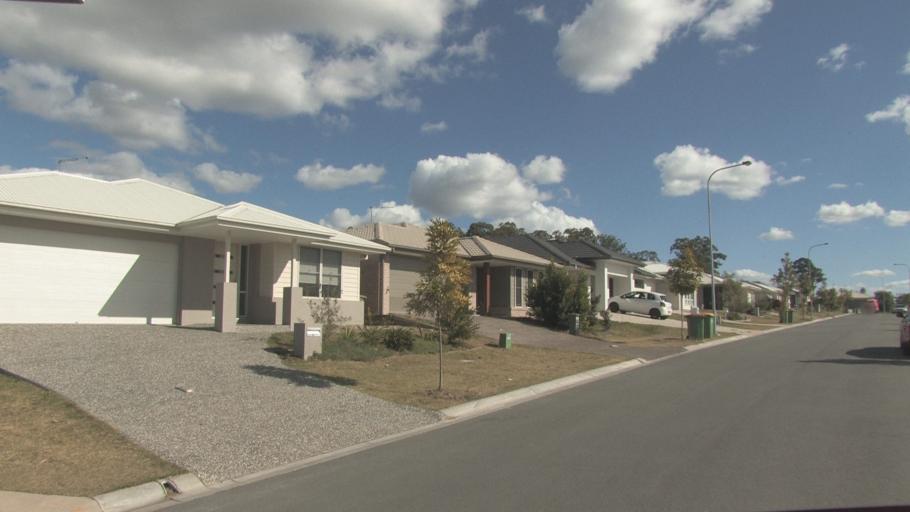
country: AU
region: Queensland
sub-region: Logan
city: Logan Reserve
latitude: -27.7166
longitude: 153.0866
